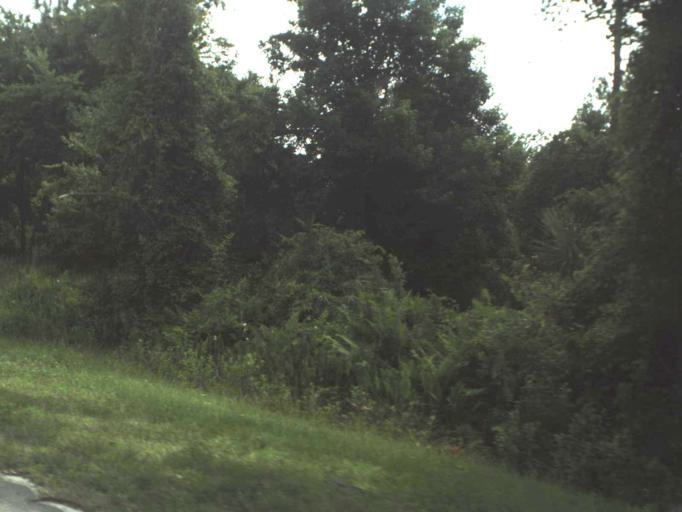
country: US
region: Florida
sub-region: Volusia County
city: Samsula-Spruce Creek
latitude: 28.9731
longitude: -81.0812
